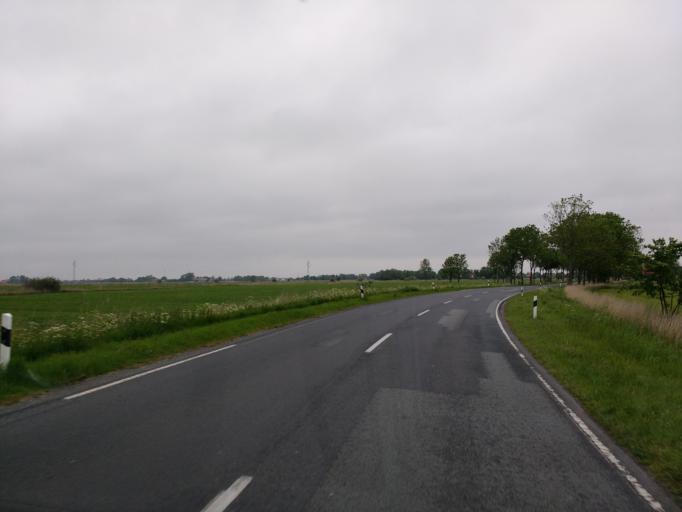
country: DE
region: Lower Saxony
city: Jever
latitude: 53.6508
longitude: 7.9186
